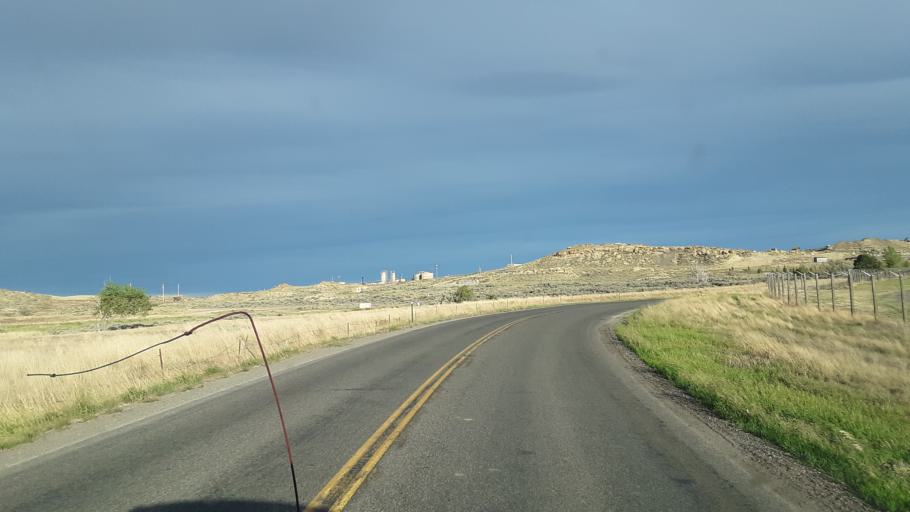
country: US
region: Wyoming
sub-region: Park County
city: Cody
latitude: 44.5290
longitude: -109.0093
